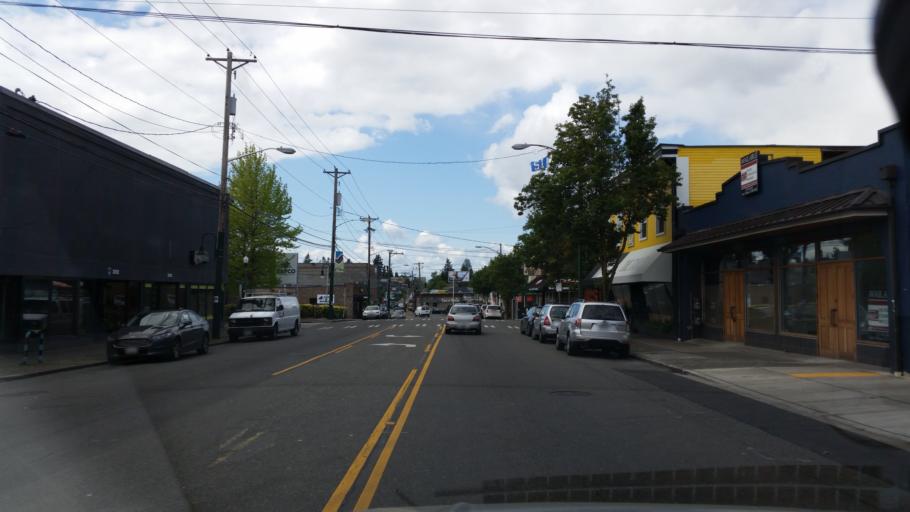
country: US
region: Washington
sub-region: Pierce County
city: Tacoma
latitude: 47.2555
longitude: -122.4712
